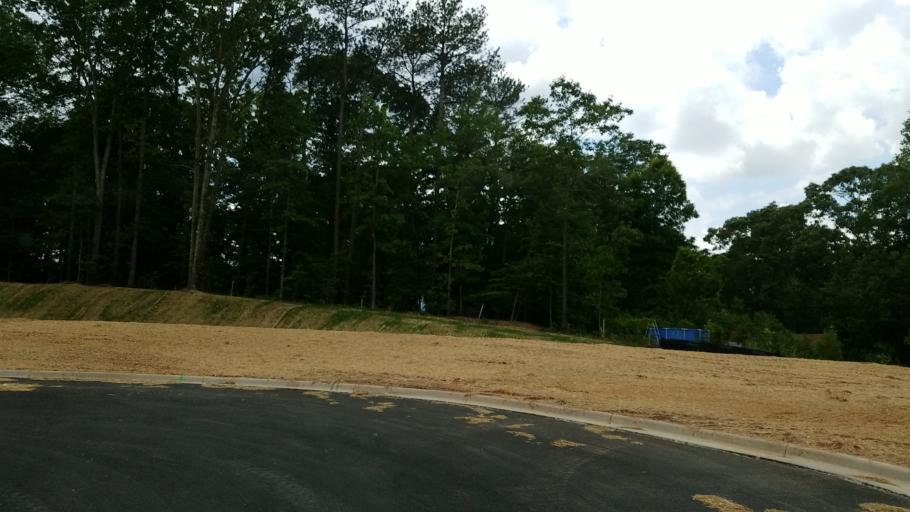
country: US
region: Georgia
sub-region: Cherokee County
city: Woodstock
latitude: 34.0166
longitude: -84.4721
